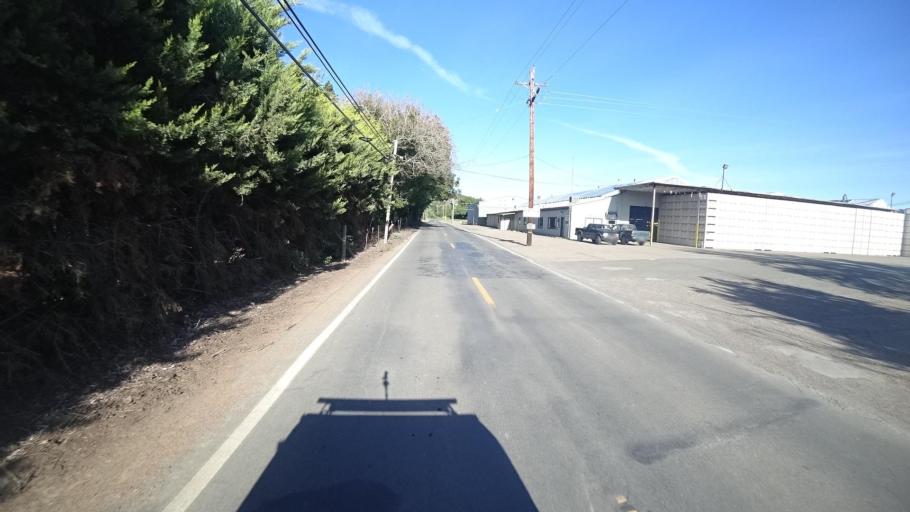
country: US
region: California
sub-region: Lake County
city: Lakeport
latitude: 39.0623
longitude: -122.9449
